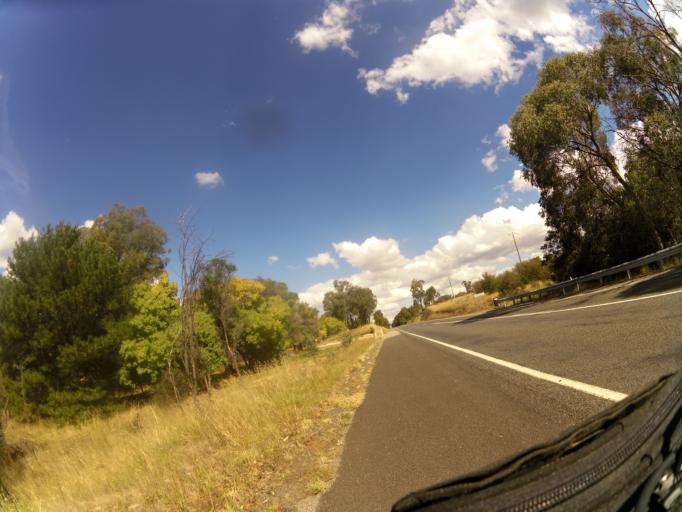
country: AU
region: Victoria
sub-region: Mansfield
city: Mansfield
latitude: -36.8796
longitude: 145.9939
